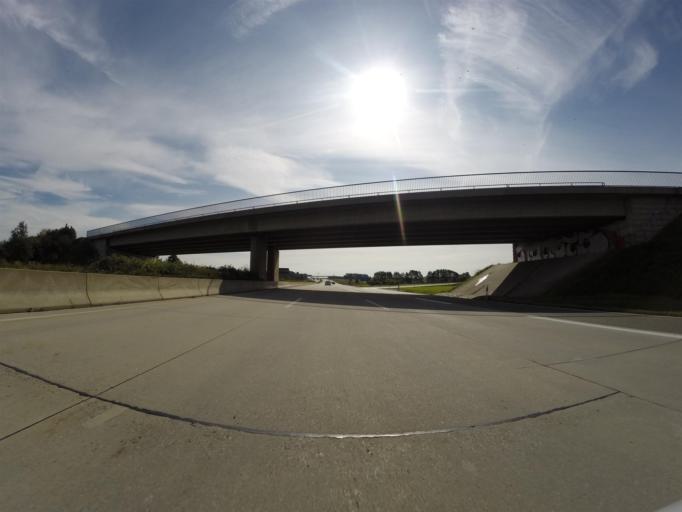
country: DE
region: Thuringia
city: Schwaara
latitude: 50.8863
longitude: 12.1503
